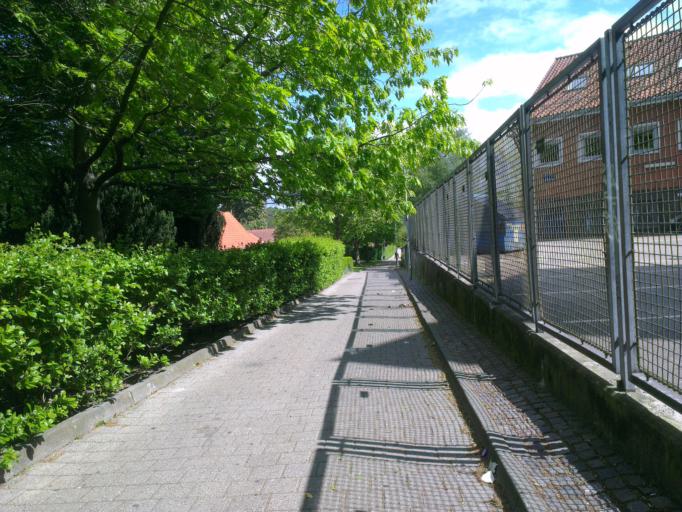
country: DK
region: Capital Region
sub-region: Hillerod Kommune
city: Hillerod
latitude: 55.9281
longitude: 12.3065
